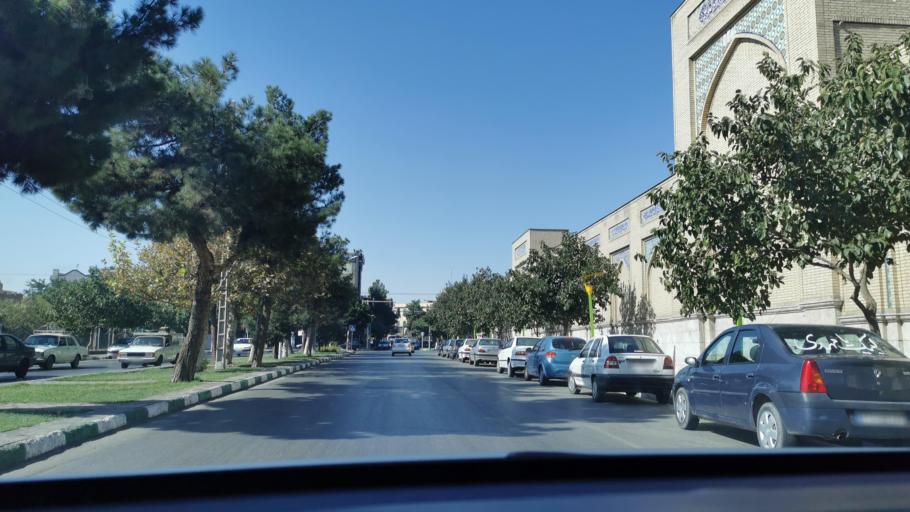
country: IR
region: Razavi Khorasan
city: Mashhad
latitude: 36.3412
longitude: 59.6302
